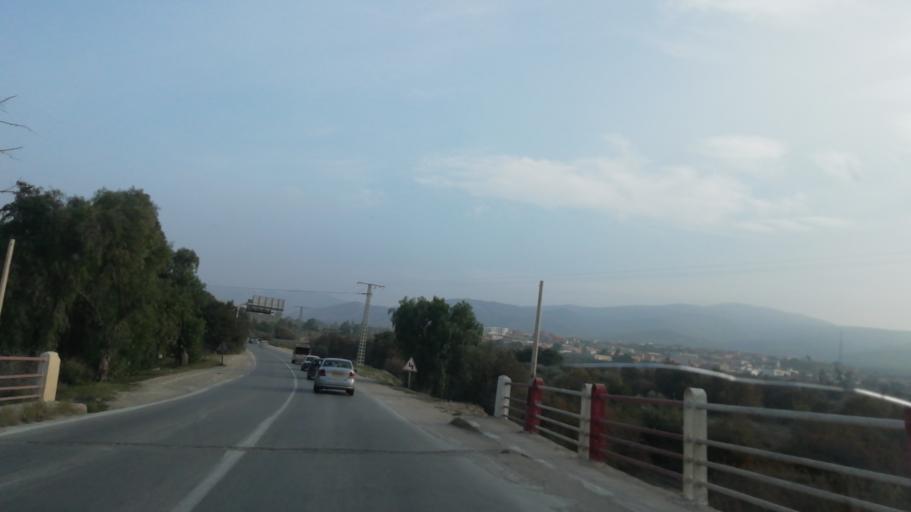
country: DZ
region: Mascara
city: Bou Hanifia el Hamamat
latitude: 35.4685
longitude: -0.0101
